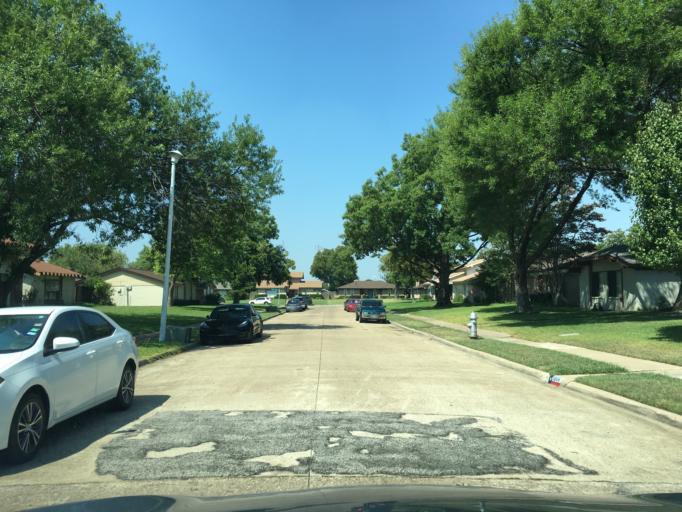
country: US
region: Texas
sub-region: Dallas County
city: Garland
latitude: 32.9330
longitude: -96.6549
